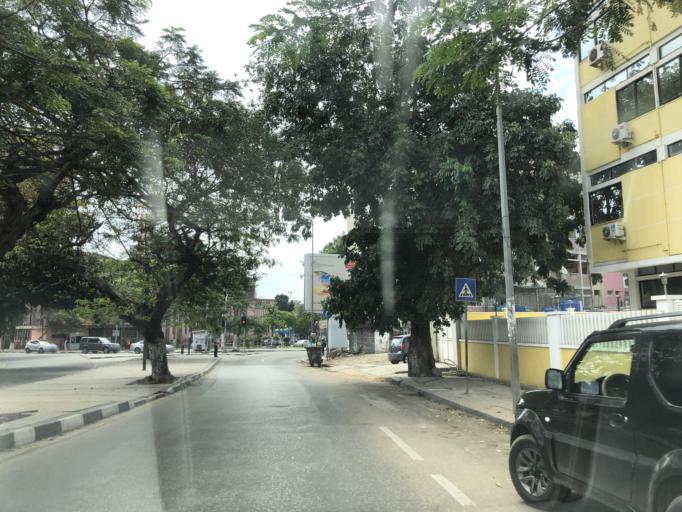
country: AO
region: Luanda
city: Luanda
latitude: -8.8247
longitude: 13.2397
